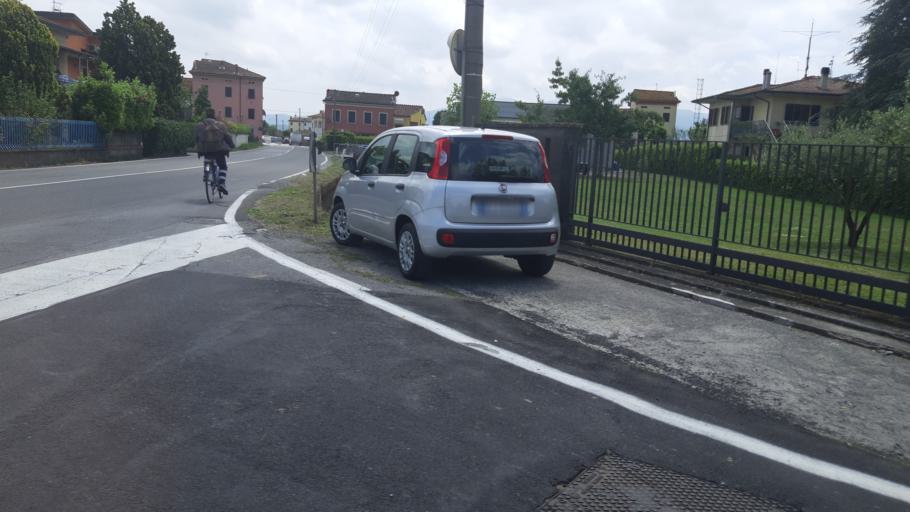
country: IT
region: Tuscany
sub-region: Provincia di Lucca
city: Capannori
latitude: 43.8643
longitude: 10.5600
